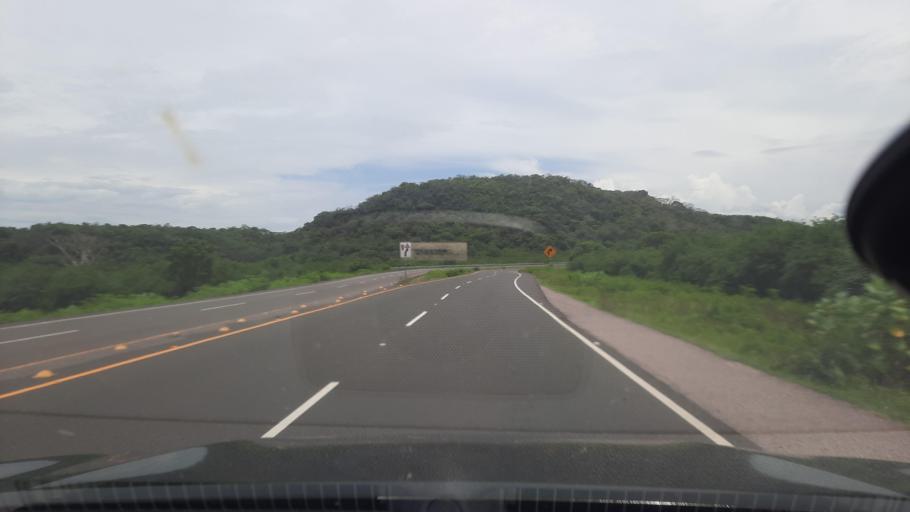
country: HN
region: Valle
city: Aramecina
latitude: 13.7281
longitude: -87.7137
